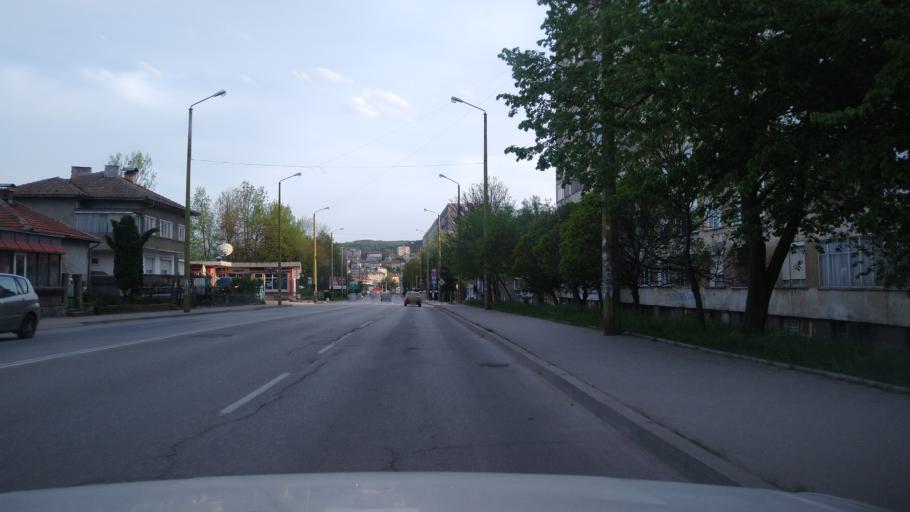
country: BG
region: Gabrovo
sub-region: Obshtina Gabrovo
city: Gabrovo
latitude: 42.8852
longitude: 25.3132
